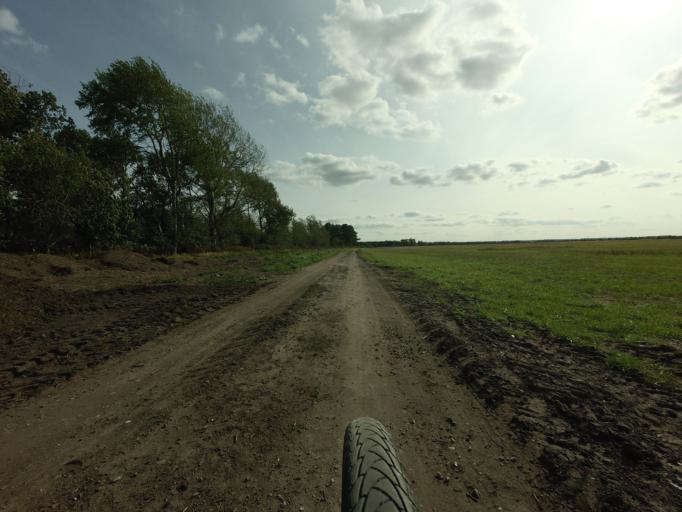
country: DK
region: Zealand
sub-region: Vordingborg Kommune
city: Praesto
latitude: 55.1486
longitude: 12.0924
